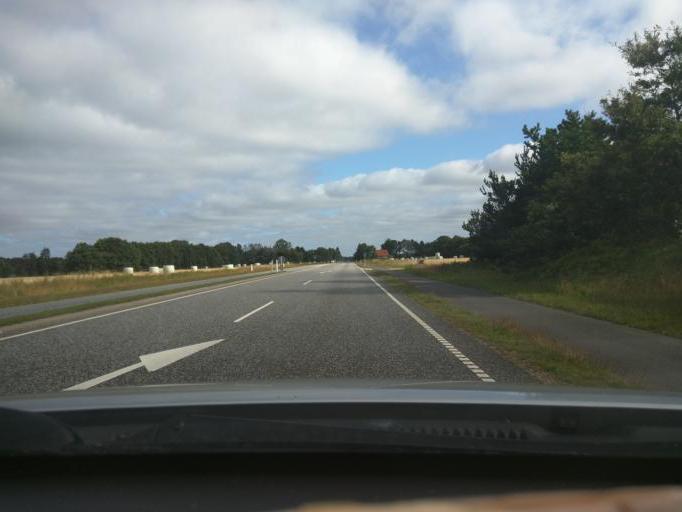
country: DK
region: Central Jutland
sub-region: Viborg Kommune
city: Viborg
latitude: 56.4101
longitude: 9.3740
